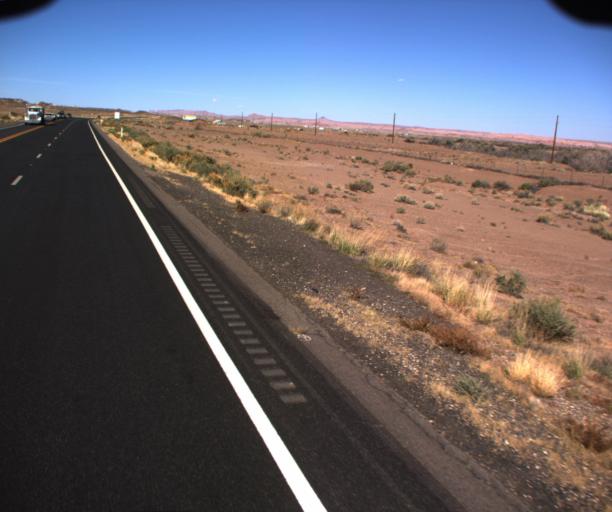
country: US
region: Arizona
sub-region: Coconino County
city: Tuba City
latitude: 36.0260
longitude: -111.3975
